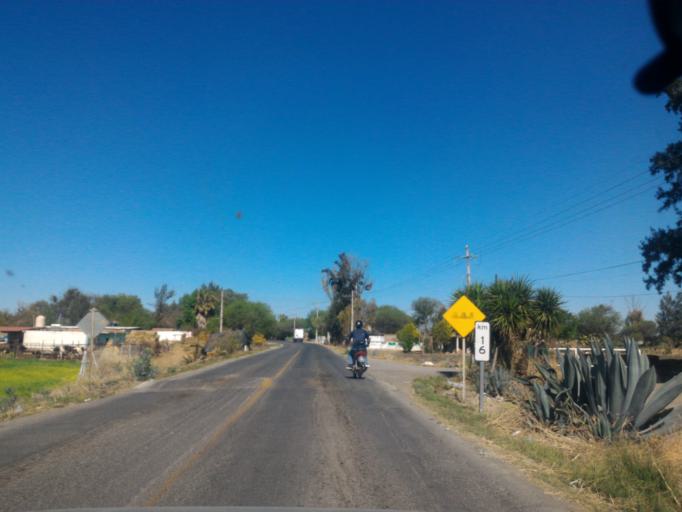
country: MX
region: Guanajuato
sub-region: San Francisco del Rincon
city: San Roque de Montes
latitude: 20.9995
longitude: -101.8082
